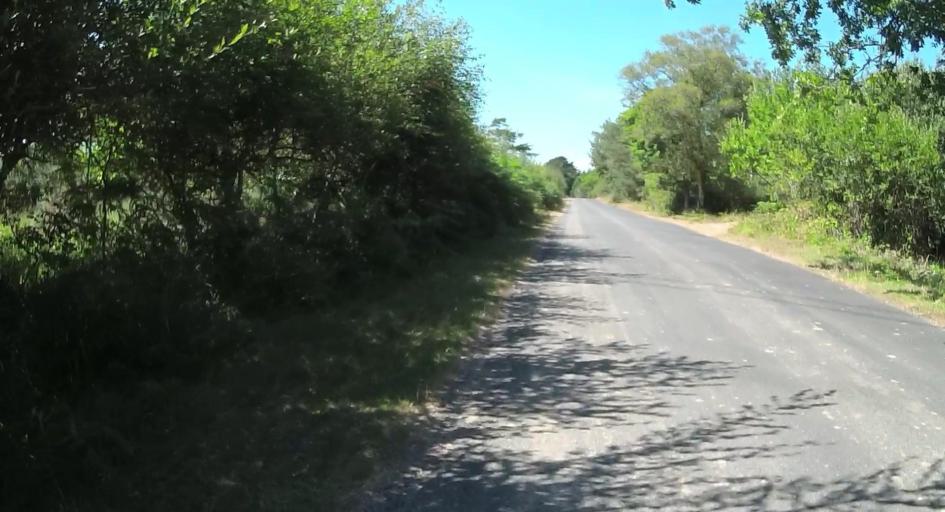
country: GB
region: England
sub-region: Dorset
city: Bovington Camp
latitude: 50.7278
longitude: -2.2562
